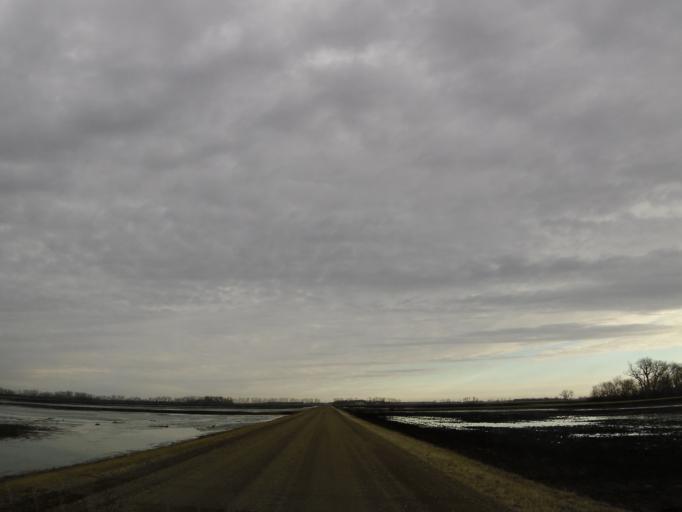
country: US
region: North Dakota
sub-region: Walsh County
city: Grafton
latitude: 48.3897
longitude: -97.4704
